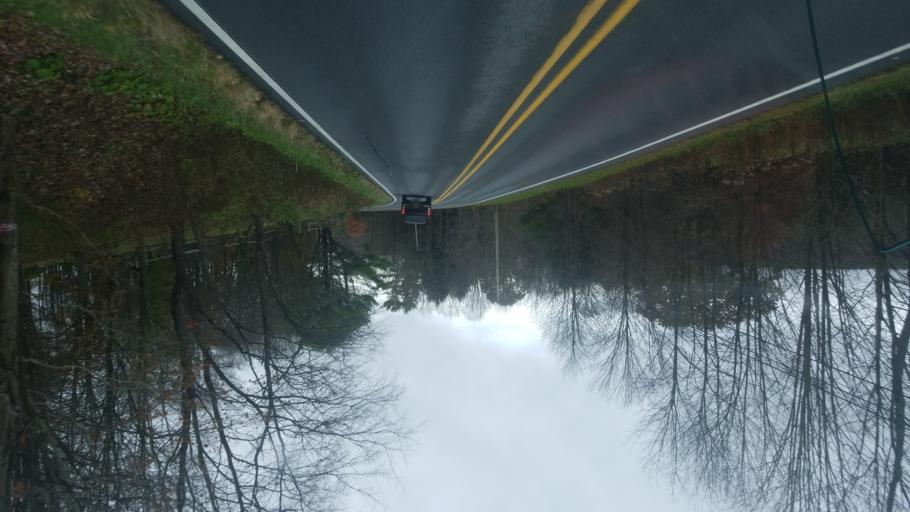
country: US
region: Pennsylvania
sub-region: Elk County
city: Ridgway
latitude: 41.3095
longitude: -78.6600
